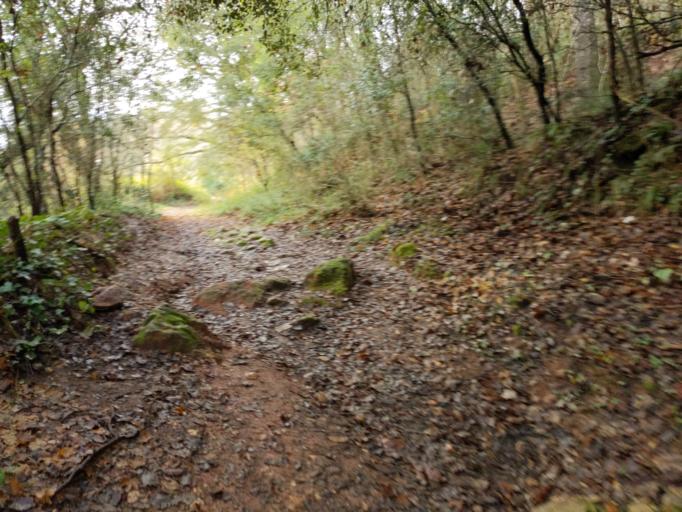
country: FR
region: Provence-Alpes-Cote d'Azur
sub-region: Departement du Var
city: Bagnols-en-Foret
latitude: 43.5402
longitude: 6.6965
